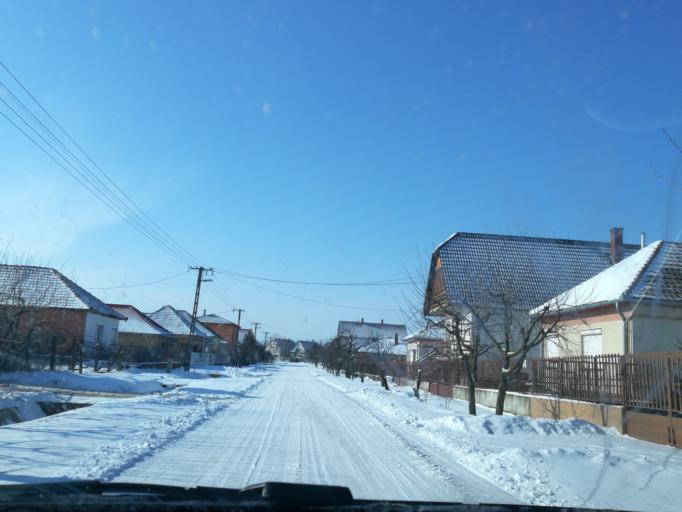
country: HU
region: Szabolcs-Szatmar-Bereg
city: Apagy
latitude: 47.9711
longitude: 21.9362
